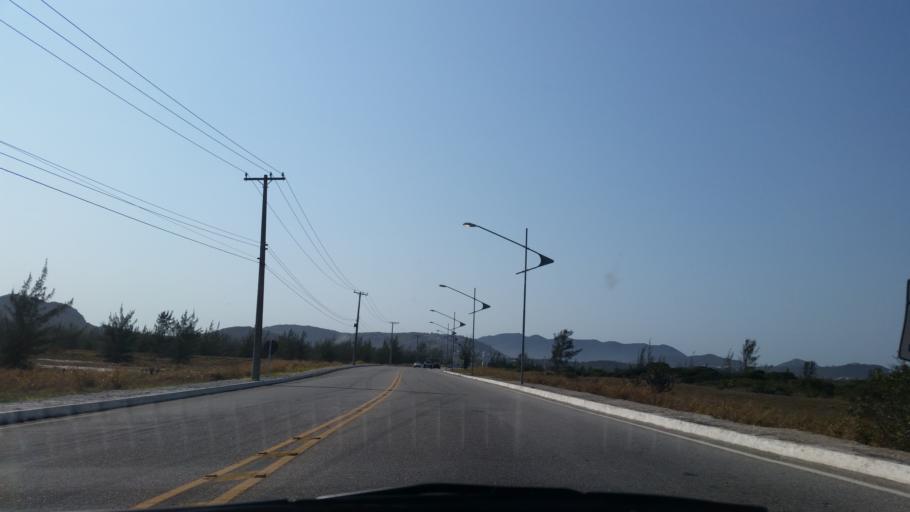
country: BR
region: Rio de Janeiro
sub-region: Arraial Do Cabo
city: Arraial do Cabo
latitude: -22.9489
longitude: -42.0484
